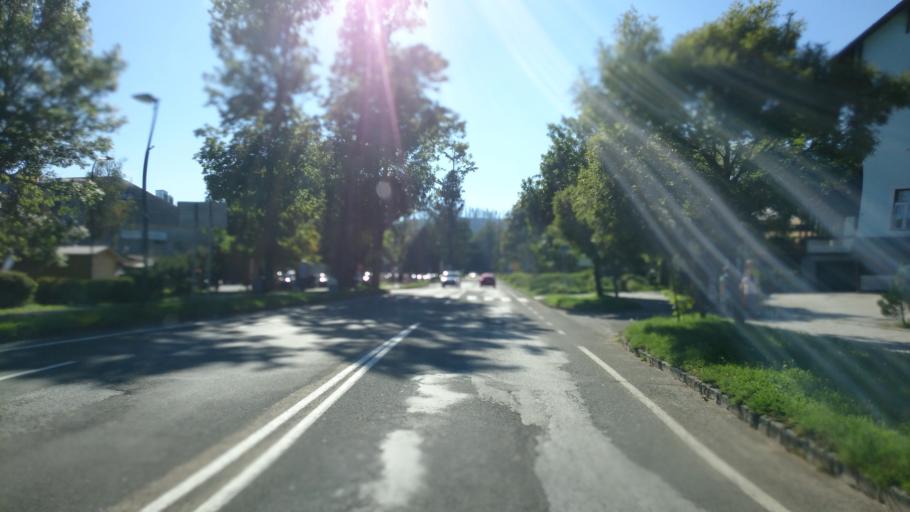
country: SK
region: Presovsky
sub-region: Okres Poprad
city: Nova Lesna
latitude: 49.1665
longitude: 20.2821
